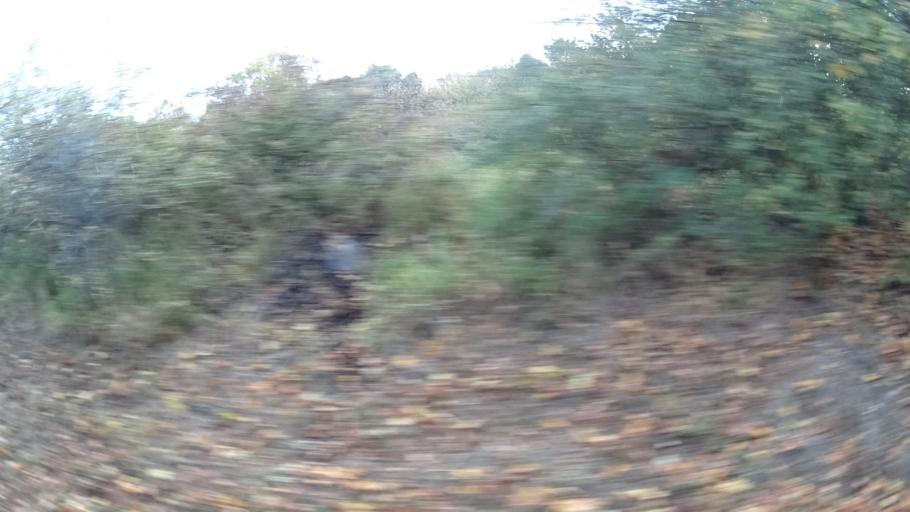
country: DE
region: Thuringia
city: Oberweid
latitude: 50.5968
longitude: 10.0708
